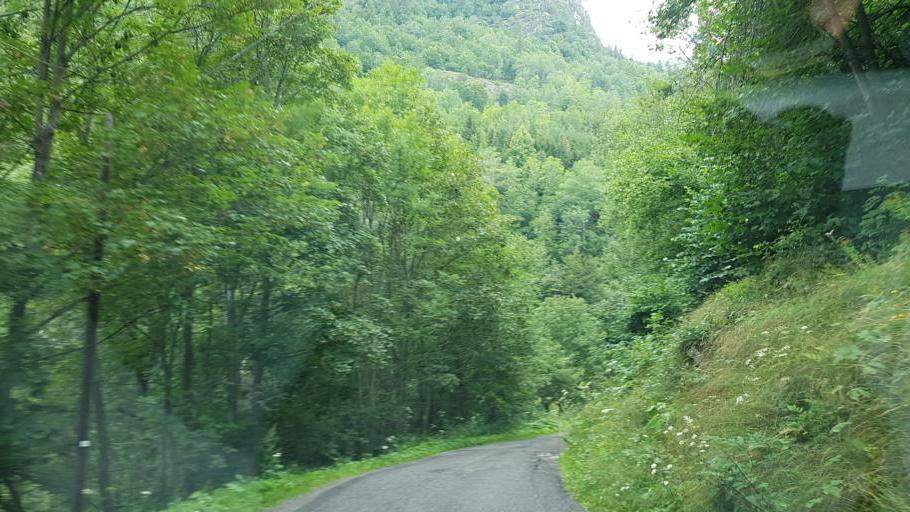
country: IT
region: Piedmont
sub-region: Provincia di Cuneo
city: Stroppo
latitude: 44.5212
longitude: 7.1243
